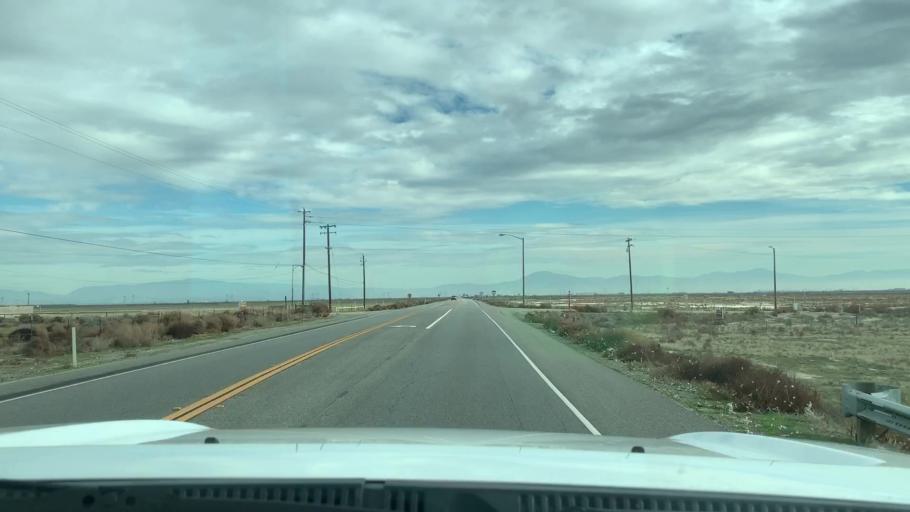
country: US
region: California
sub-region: Kern County
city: Rosedale
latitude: 35.2675
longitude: -119.2896
